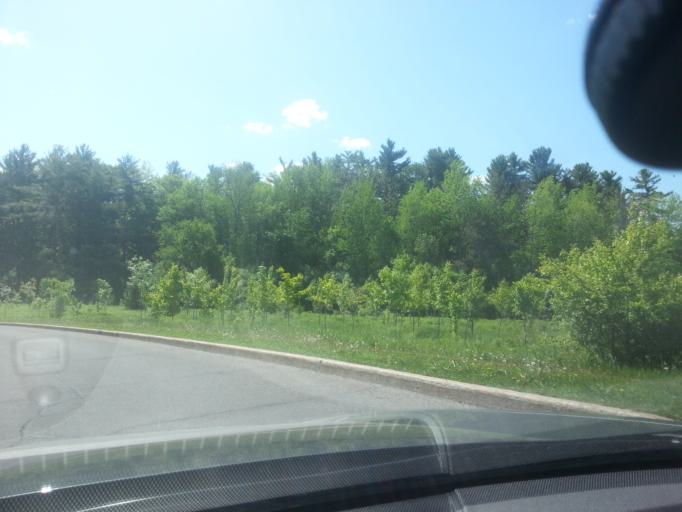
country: CA
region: Ontario
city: Ottawa
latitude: 45.4383
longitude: -75.7610
